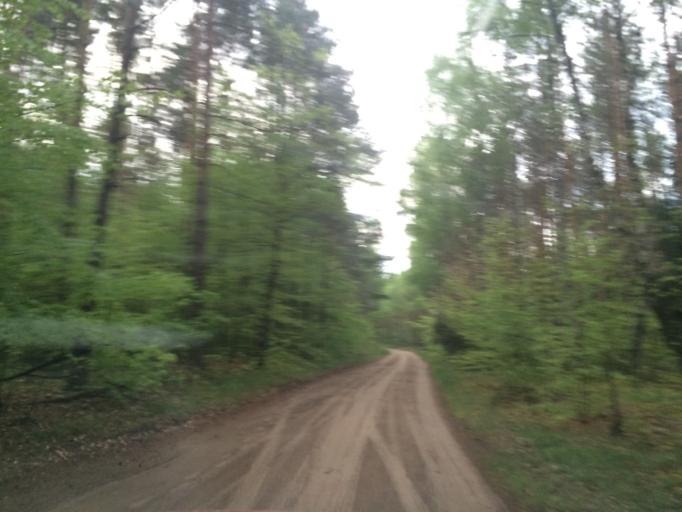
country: PL
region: Warmian-Masurian Voivodeship
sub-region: Powiat nowomiejski
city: Kurzetnik
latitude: 53.3568
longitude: 19.5181
